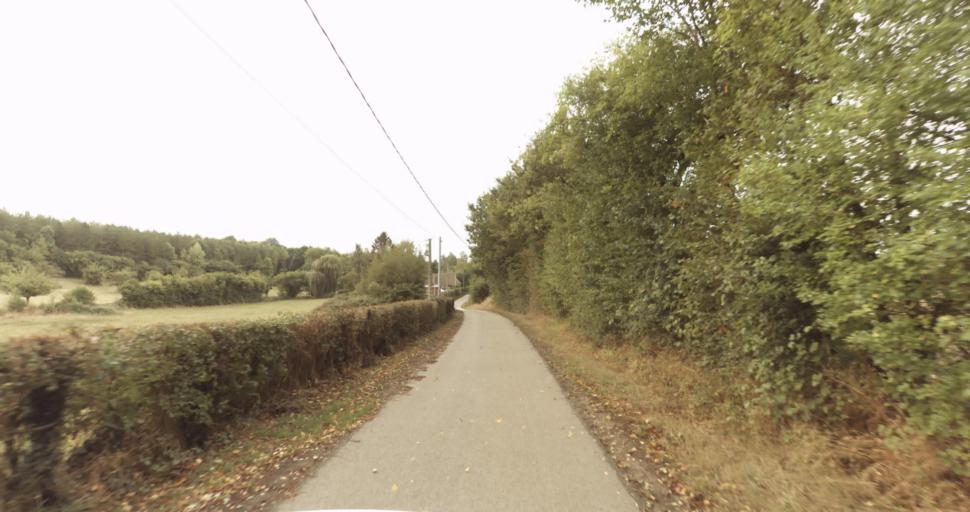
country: FR
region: Lower Normandy
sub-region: Departement de l'Orne
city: Trun
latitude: 48.9177
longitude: 0.0929
